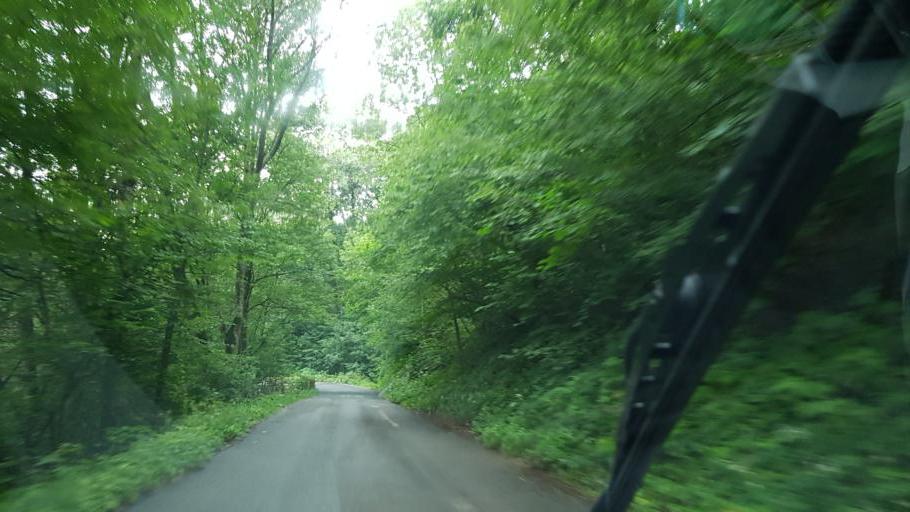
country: IT
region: Piedmont
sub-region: Provincia di Cuneo
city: Sampeyre
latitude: 44.5763
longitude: 7.1753
